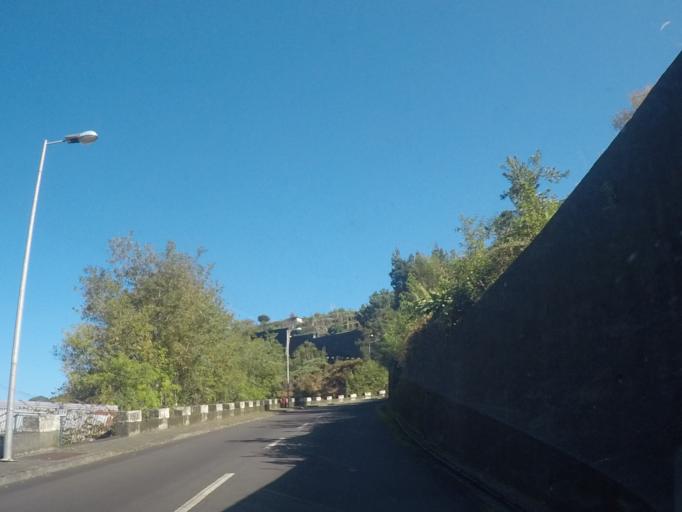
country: PT
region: Madeira
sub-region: Santana
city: Santana
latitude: 32.8011
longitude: -16.9629
